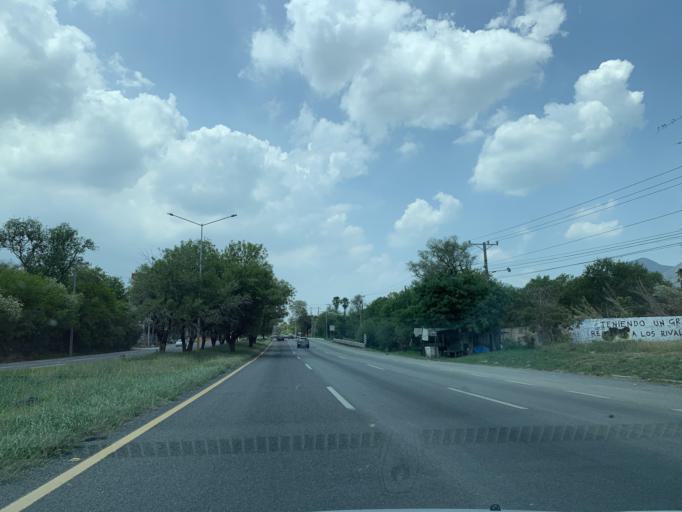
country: MX
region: Nuevo Leon
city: Santiago
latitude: 25.4425
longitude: -100.1555
